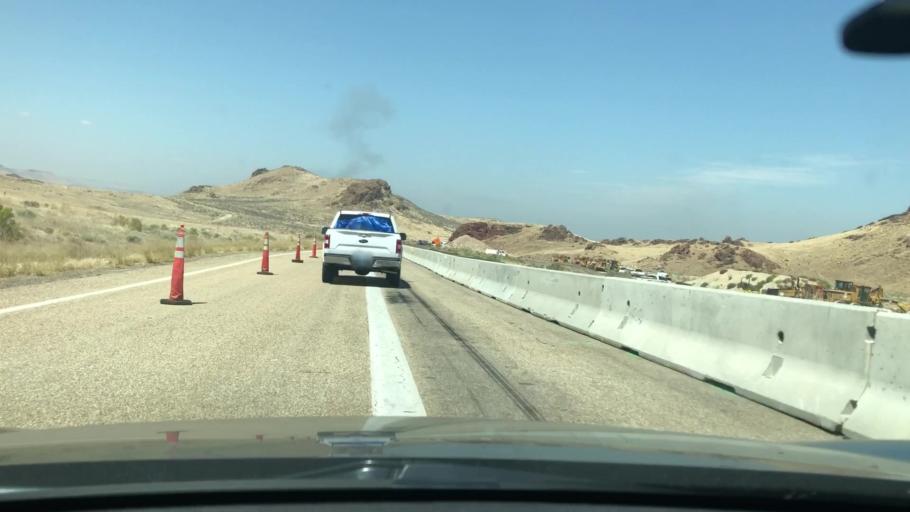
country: US
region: Idaho
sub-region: Owyhee County
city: Marsing
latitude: 43.4553
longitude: -116.8624
